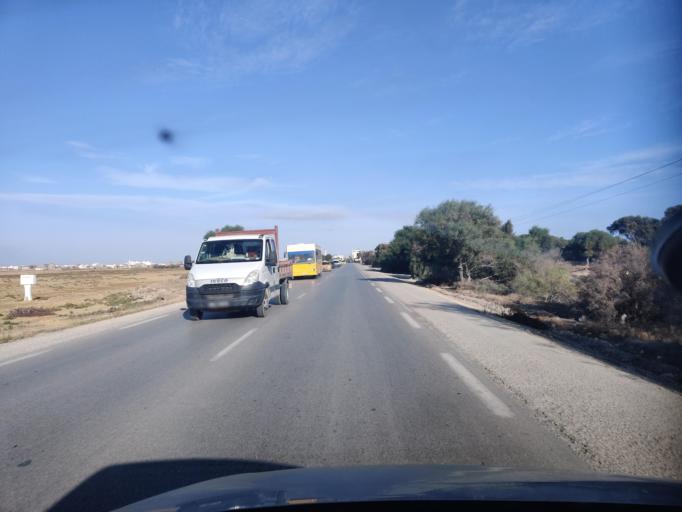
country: TN
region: Ariana
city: Ariana
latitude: 36.9501
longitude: 10.2377
